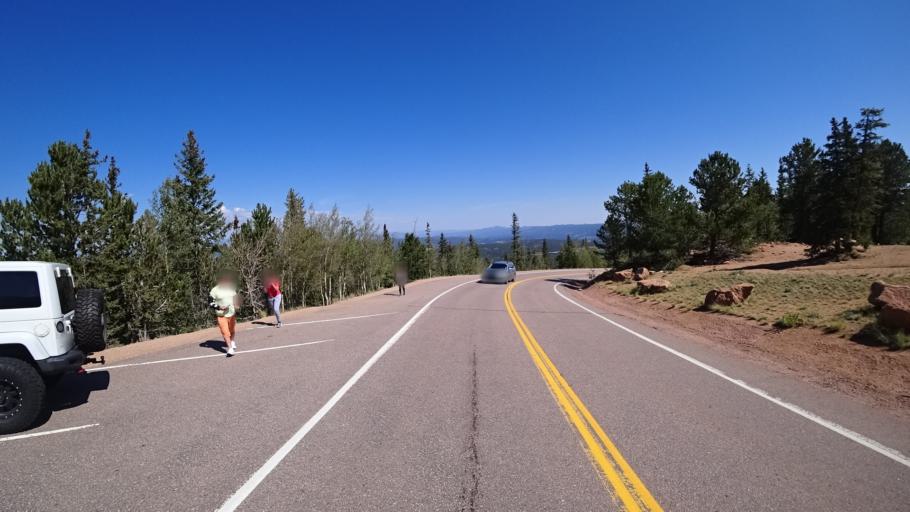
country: US
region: Colorado
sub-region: El Paso County
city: Cascade-Chipita Park
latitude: 38.8928
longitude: -105.0687
